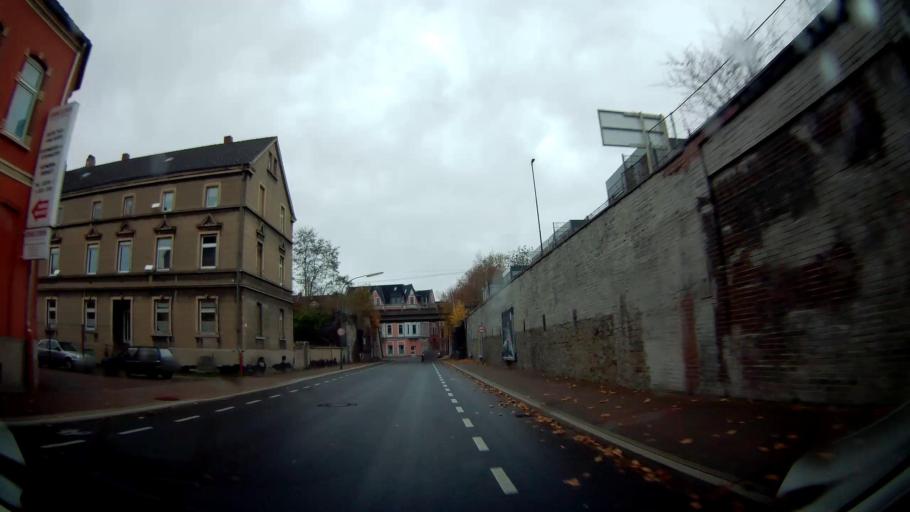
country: DE
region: North Rhine-Westphalia
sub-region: Regierungsbezirk Munster
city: Gelsenkirchen
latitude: 51.4997
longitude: 7.0807
